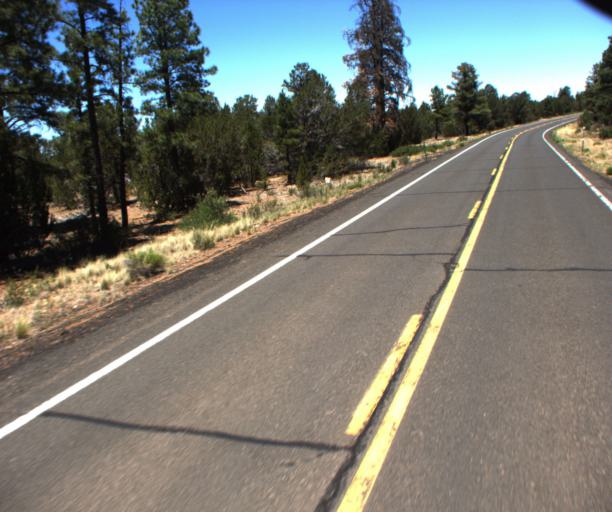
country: US
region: Arizona
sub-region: Gila County
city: Star Valley
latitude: 34.6991
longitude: -111.1057
